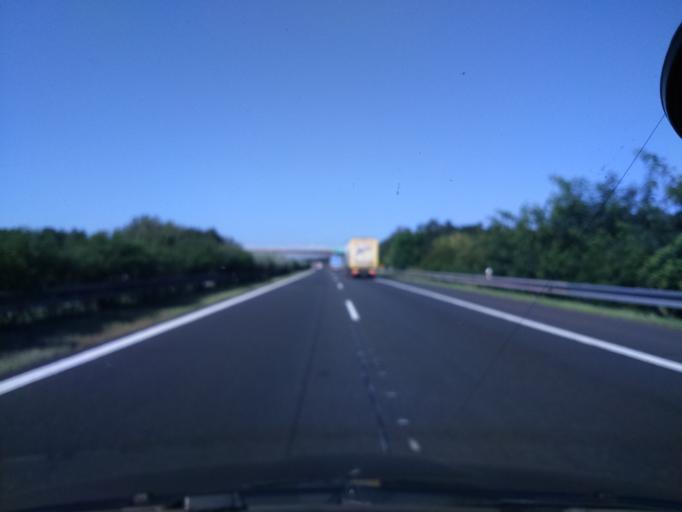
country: CZ
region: Central Bohemia
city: Pecky
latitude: 50.1237
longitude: 15.0315
